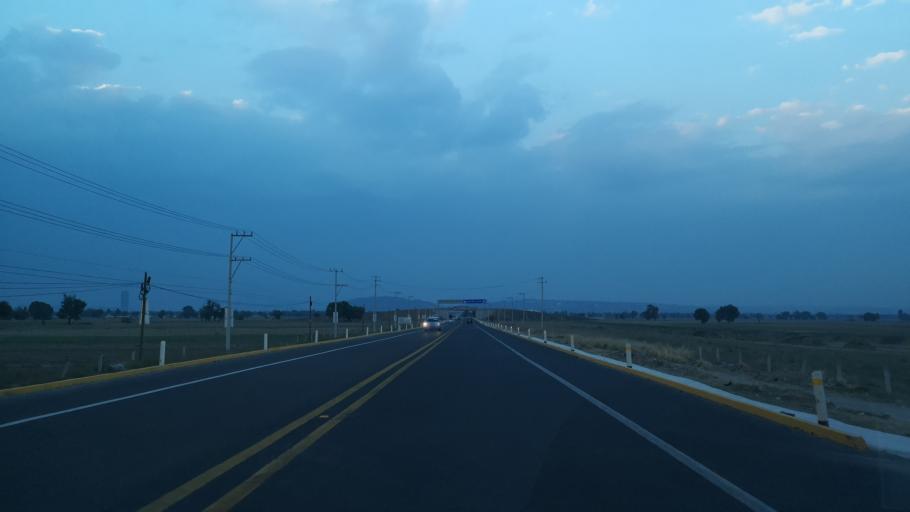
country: MX
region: Puebla
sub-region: Huejotzingo
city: Los Encinos
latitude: 19.1824
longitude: -98.3716
